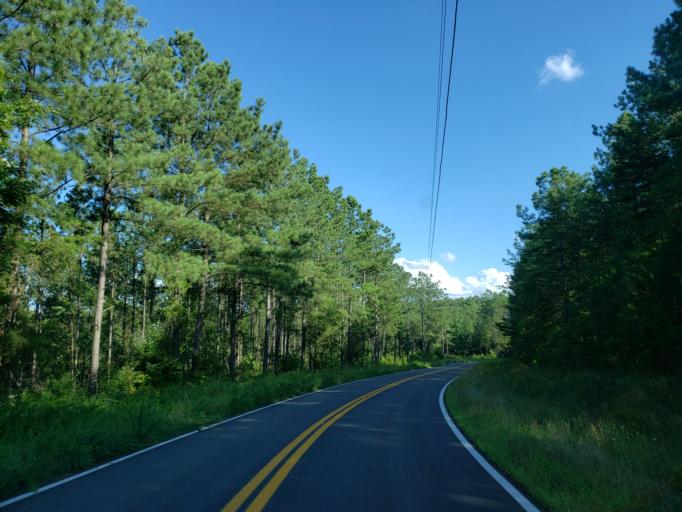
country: US
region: Georgia
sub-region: Bartow County
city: Rydal
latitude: 34.3729
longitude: -84.6264
